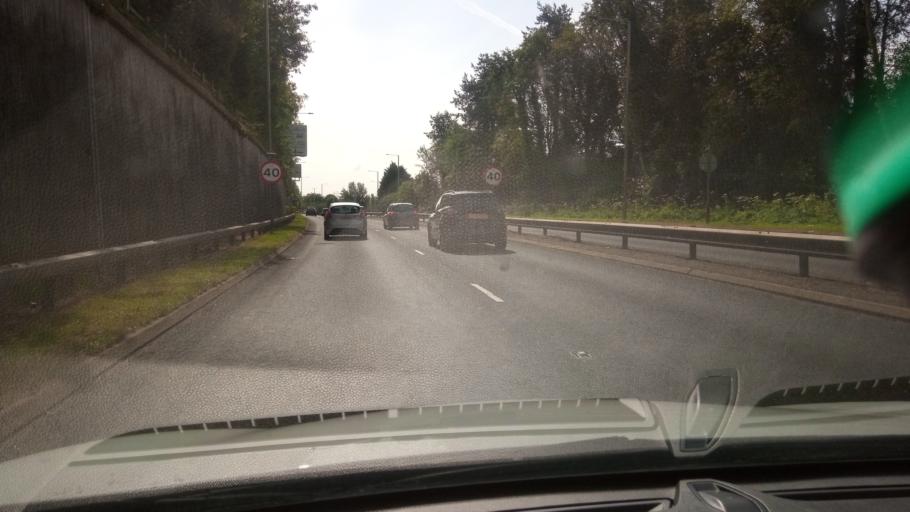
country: GB
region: Wales
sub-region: Rhondda Cynon Taf
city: Llantrisant
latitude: 51.5403
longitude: -3.3837
